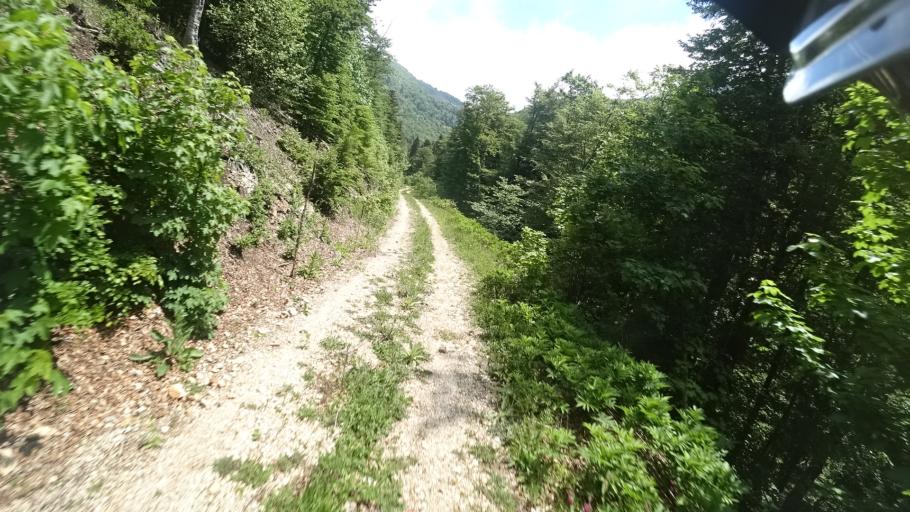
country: BA
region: Federation of Bosnia and Herzegovina
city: Orasac
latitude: 44.5638
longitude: 15.8582
